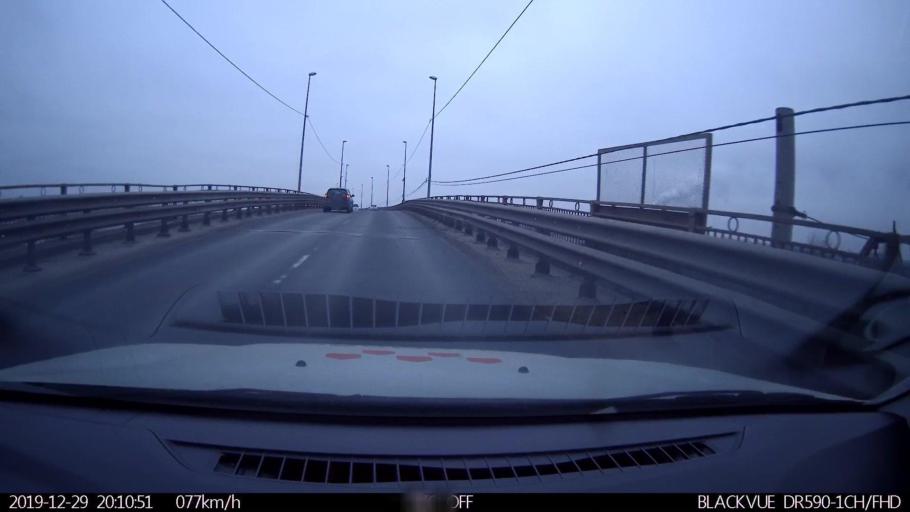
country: RU
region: Nizjnij Novgorod
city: Neklyudovo
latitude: 56.3616
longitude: 43.9310
